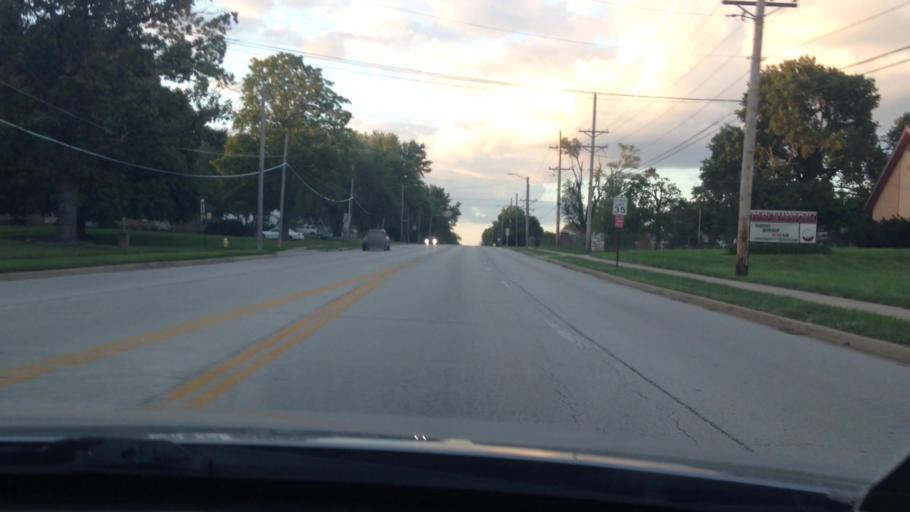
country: US
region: Missouri
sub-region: Jackson County
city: Raytown
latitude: 38.9733
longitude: -94.4650
